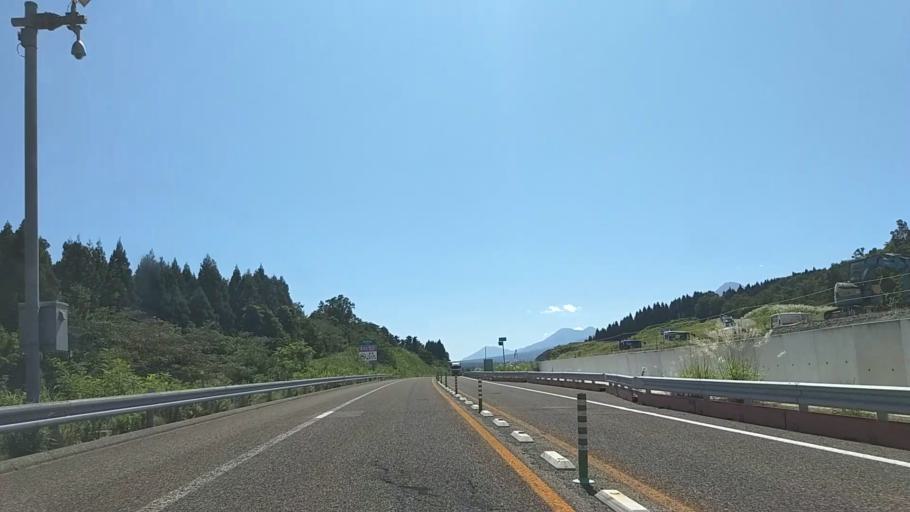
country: JP
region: Niigata
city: Arai
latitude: 37.0386
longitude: 138.2321
